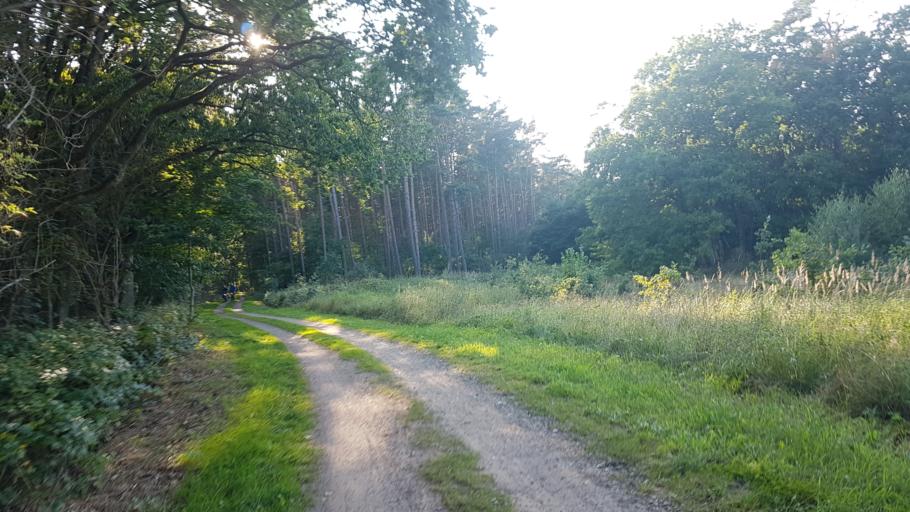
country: DE
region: Mecklenburg-Vorpommern
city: Ostseebad Binz
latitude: 54.3604
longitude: 13.6165
